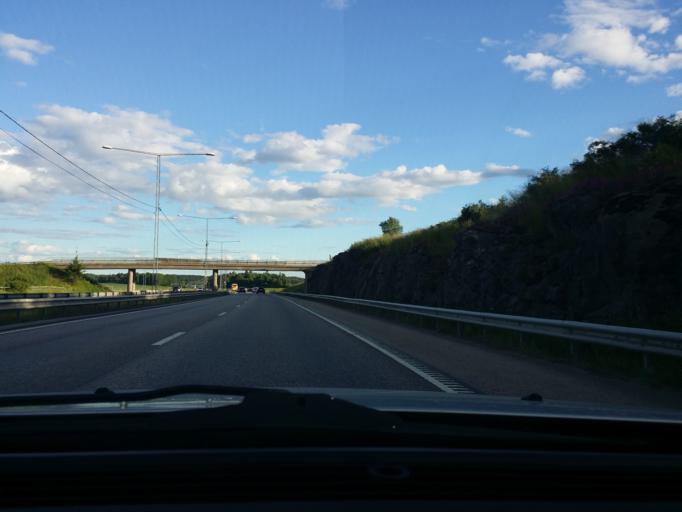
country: SE
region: Stockholm
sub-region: Sigtuna Kommun
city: Rosersberg
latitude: 59.5689
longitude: 17.8974
